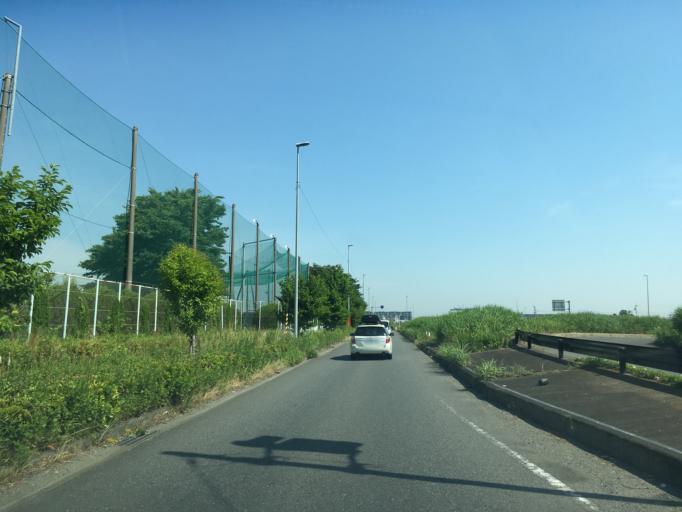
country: JP
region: Saitama
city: Yoshikawa
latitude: 35.8656
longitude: 139.8286
